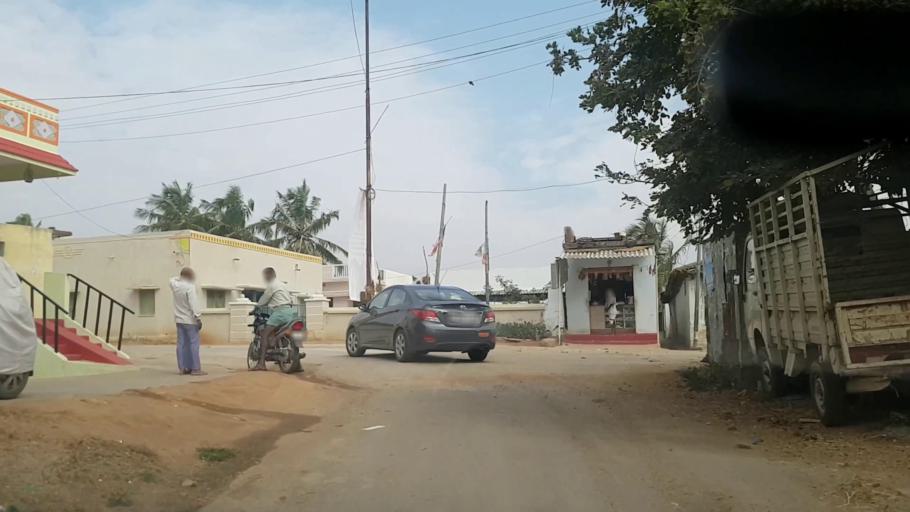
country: IN
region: Telangana
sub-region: Rangareddi
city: Lal Bahadur Nagar
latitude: 17.1665
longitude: 78.7848
